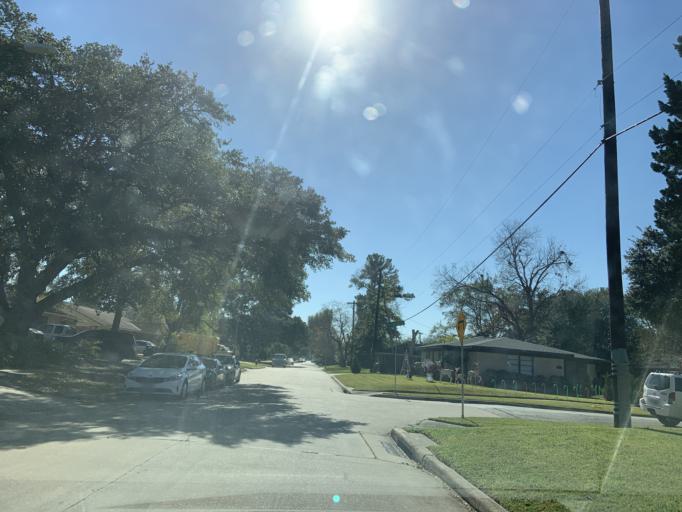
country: US
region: Texas
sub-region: Harris County
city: Bellaire
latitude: 29.6833
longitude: -95.5058
